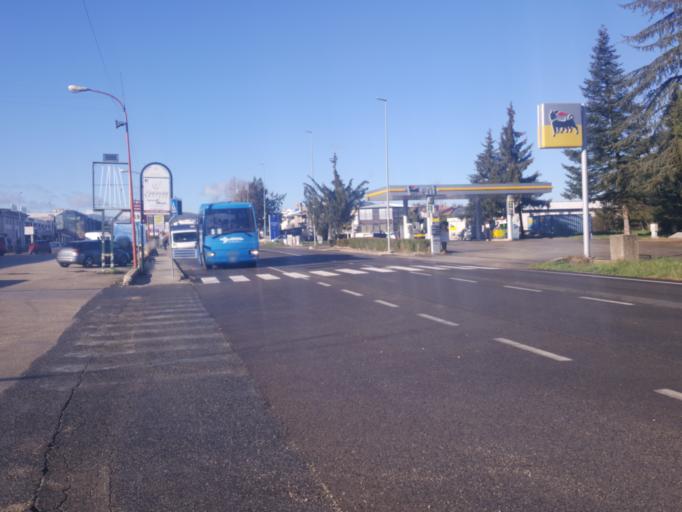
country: IT
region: Abruzzo
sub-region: Provincia dell' Aquila
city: Carsoli
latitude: 42.0856
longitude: 13.0635
